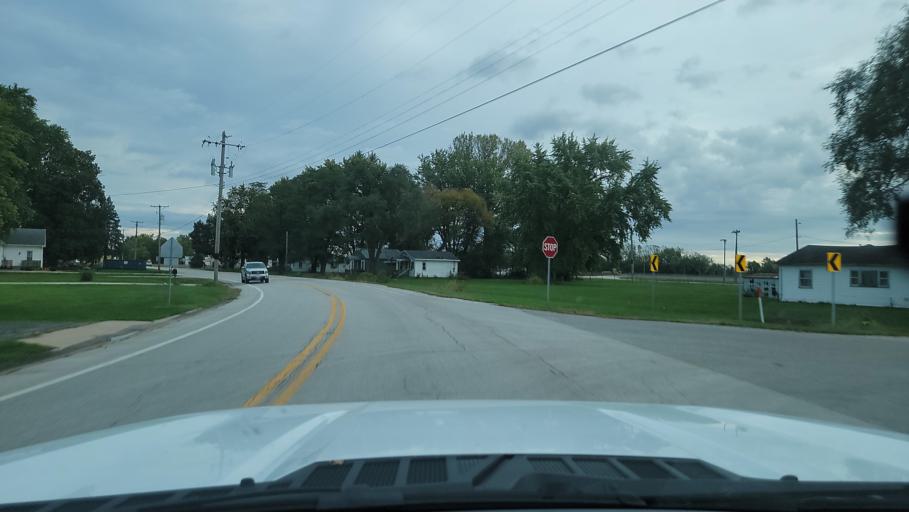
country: US
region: Illinois
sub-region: Schuyler County
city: Rushville
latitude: 40.1299
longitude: -90.5626
